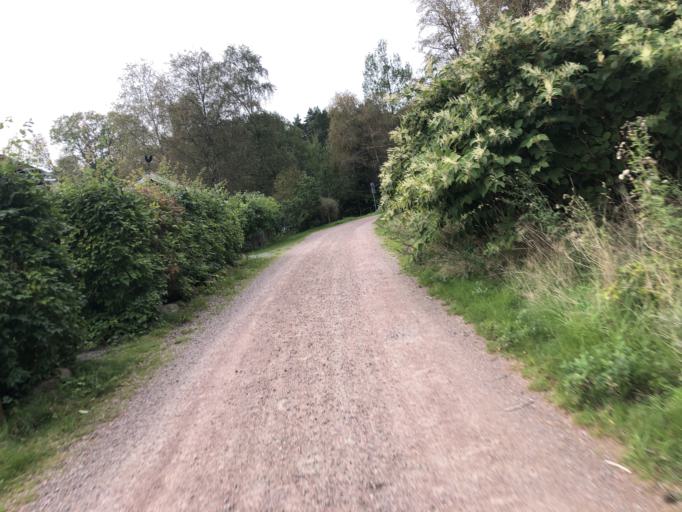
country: SE
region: Vaestra Goetaland
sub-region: Goteborg
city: Majorna
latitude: 57.7502
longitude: 11.9006
